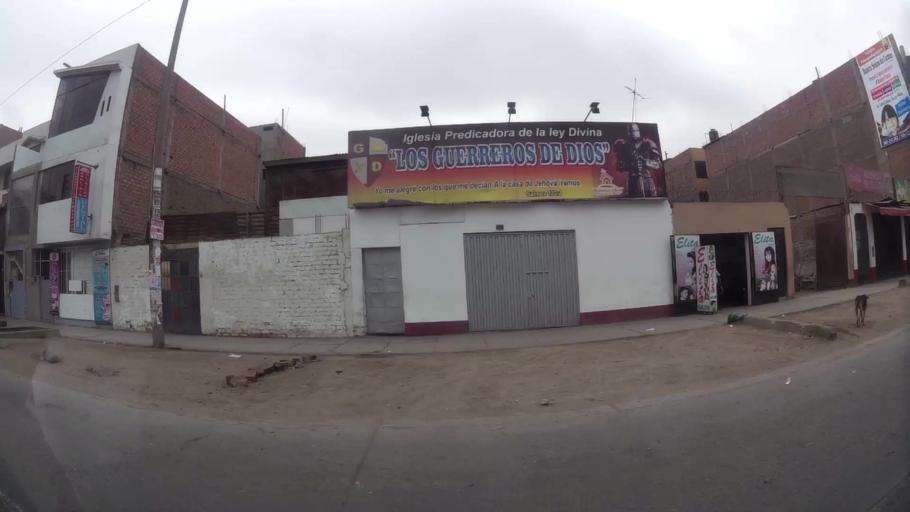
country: PE
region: Lima
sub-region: Lima
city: Independencia
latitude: -11.9752
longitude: -77.0827
